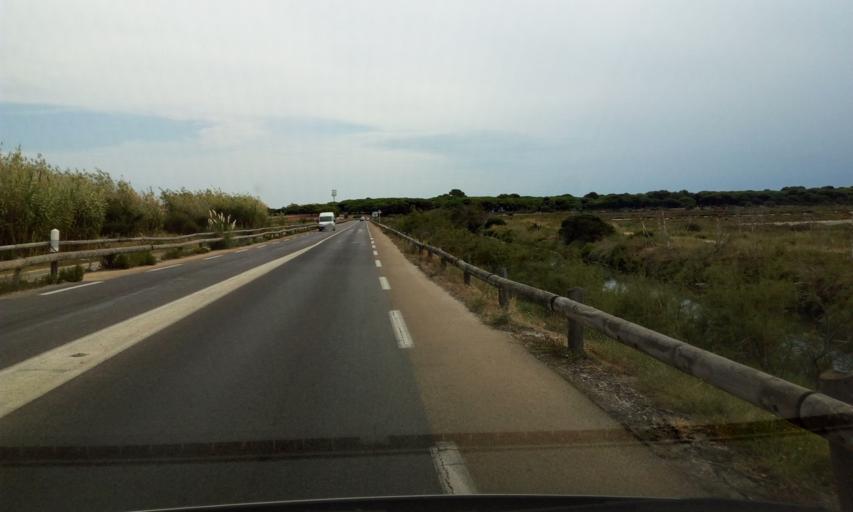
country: FR
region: Provence-Alpes-Cote d'Azur
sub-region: Departement du Var
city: Hyeres
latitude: 43.0820
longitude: 6.1442
